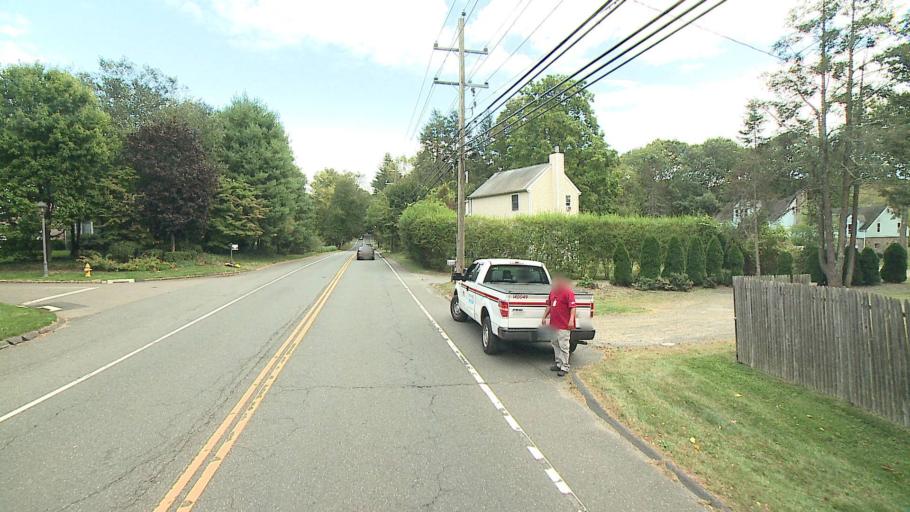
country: US
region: Connecticut
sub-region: Fairfield County
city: Wilton
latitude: 41.1789
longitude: -73.4051
